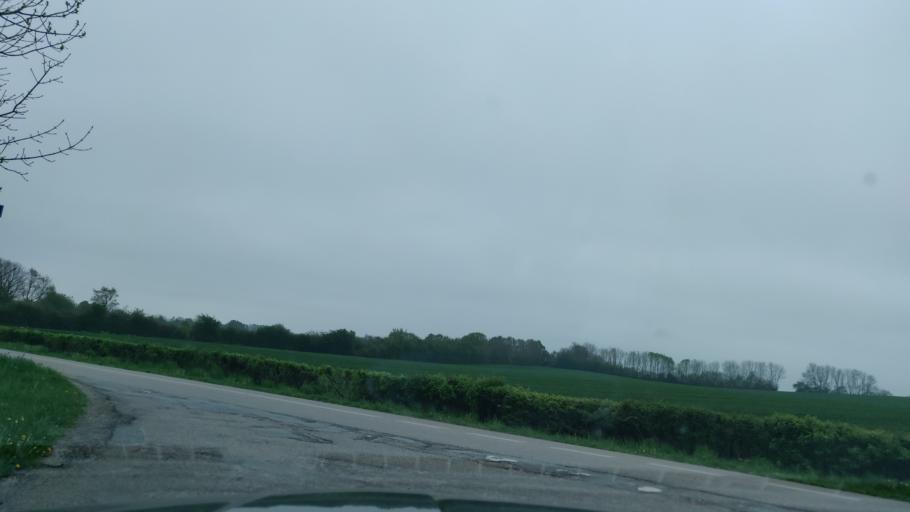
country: DK
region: South Denmark
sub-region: Sonderborg Kommune
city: Guderup
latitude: 54.9996
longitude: 9.9524
